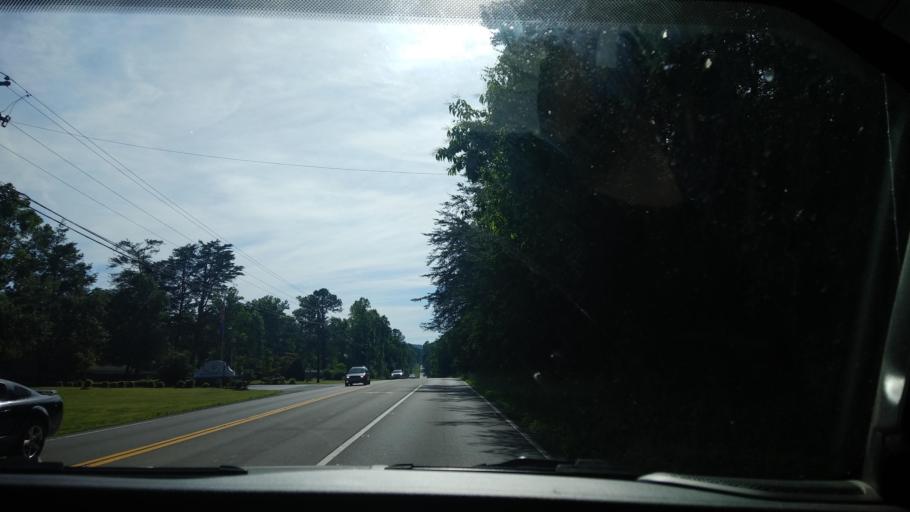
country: US
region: Tennessee
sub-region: Sevier County
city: Gatlinburg
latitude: 35.7595
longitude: -83.3458
